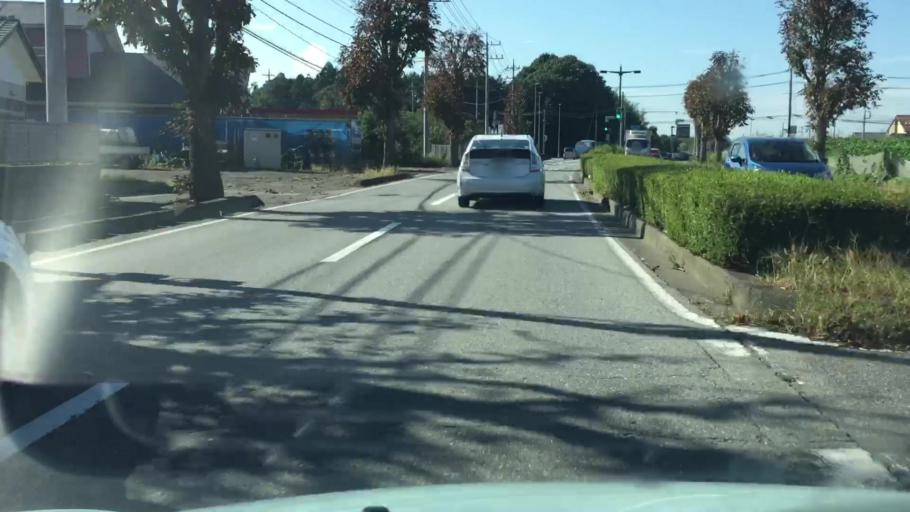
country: JP
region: Tochigi
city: Mooka
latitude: 36.5340
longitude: 139.9885
